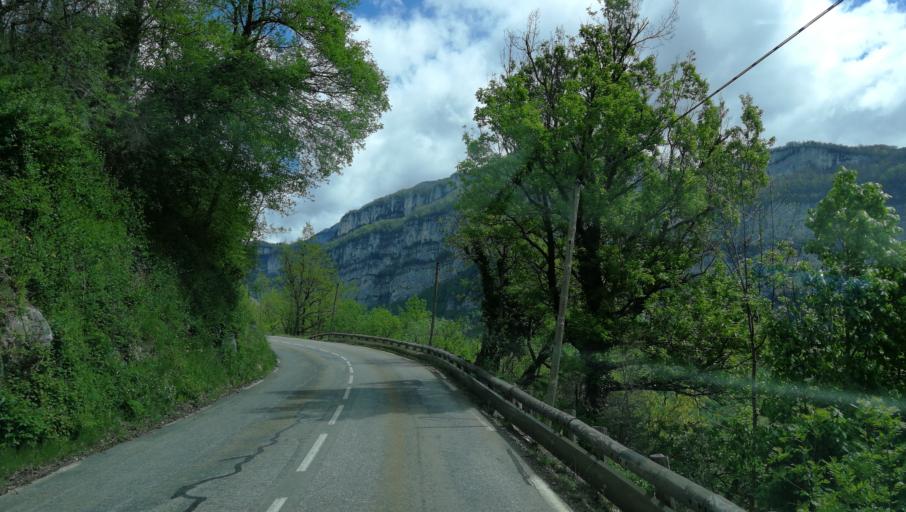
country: FR
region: Rhone-Alpes
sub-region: Departement de l'Isere
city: Pont-en-Royans
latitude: 45.0610
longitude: 5.4181
